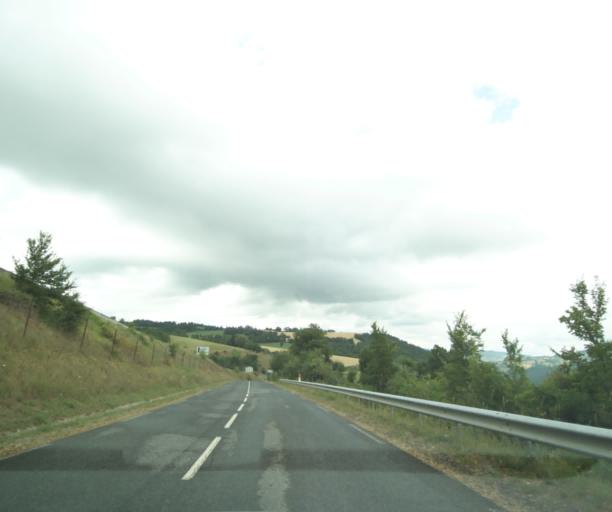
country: FR
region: Languedoc-Roussillon
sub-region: Departement de la Lozere
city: La Canourgue
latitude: 44.4205
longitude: 3.1847
